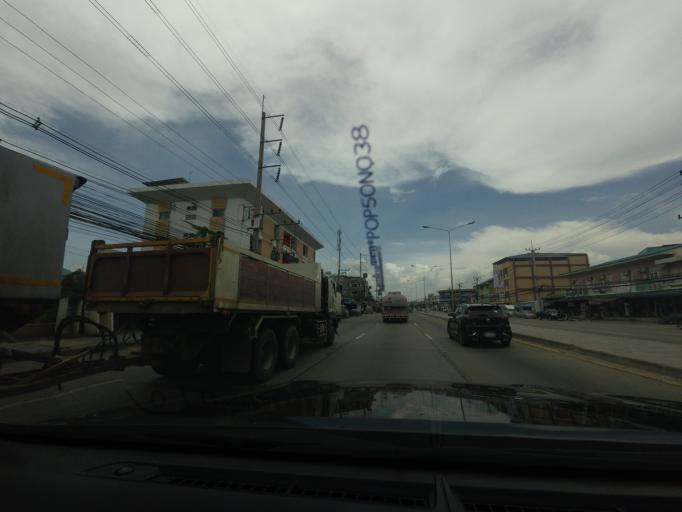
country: TH
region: Nakhon Pathom
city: Nakhon Pathom
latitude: 13.8398
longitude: 100.0287
